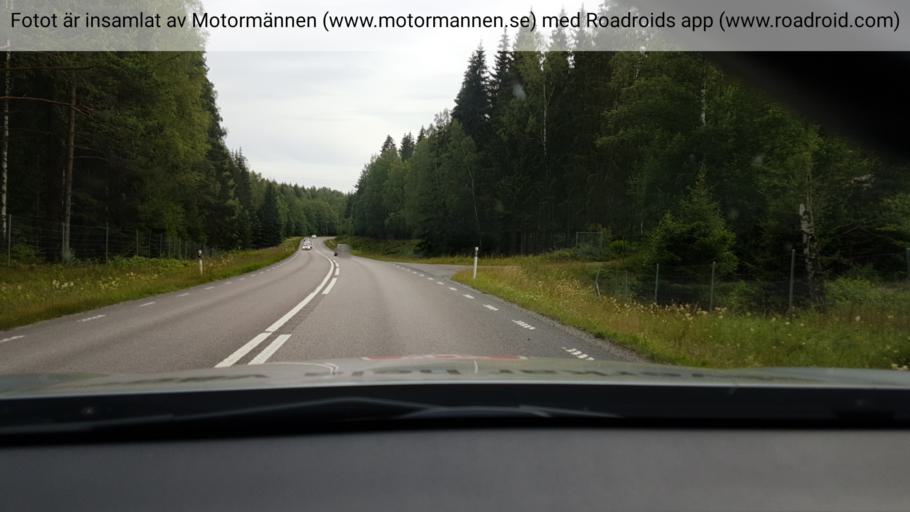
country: SE
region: Vaestra Goetaland
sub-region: Bengtsfors Kommun
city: Billingsfors
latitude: 58.9976
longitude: 12.2696
